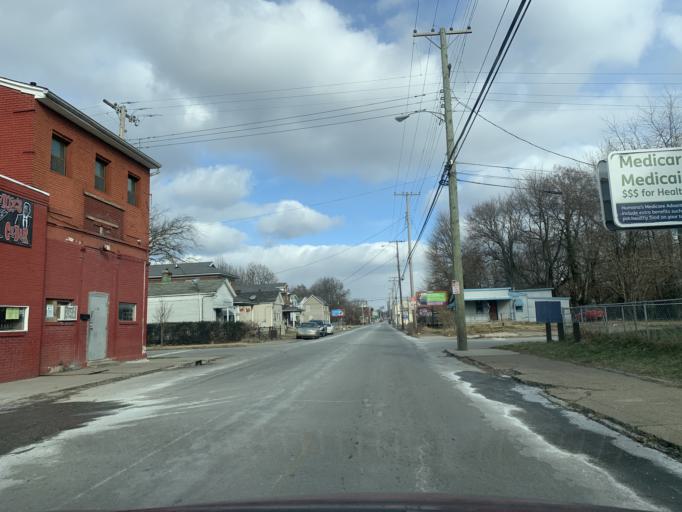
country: US
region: Kentucky
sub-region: Jefferson County
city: Louisville
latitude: 38.2563
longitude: -85.7941
